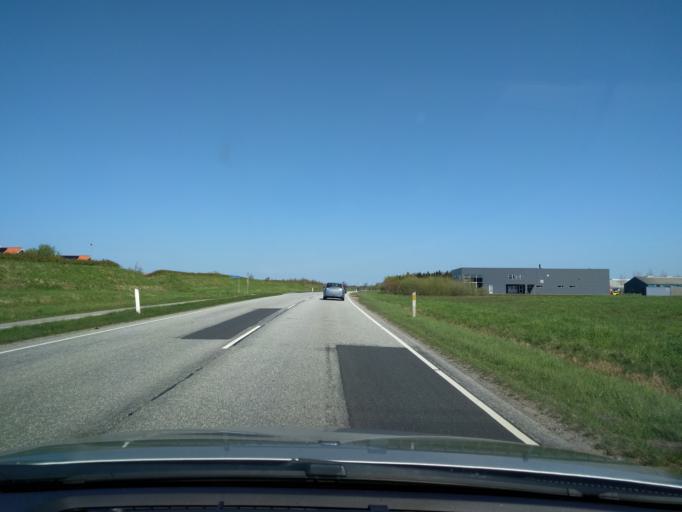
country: DK
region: Central Jutland
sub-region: Ringkobing-Skjern Kommune
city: Ringkobing
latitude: 56.0926
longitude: 8.2776
